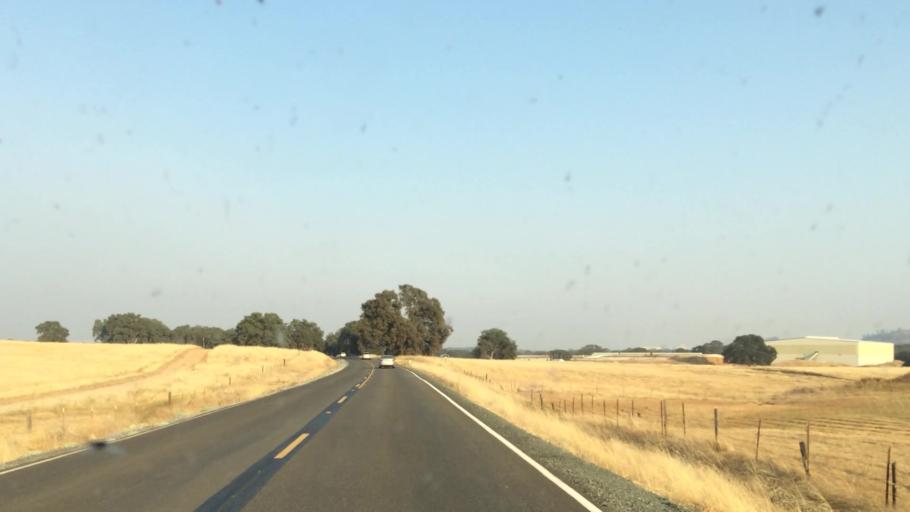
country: US
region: California
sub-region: Amador County
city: Ione
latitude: 38.4004
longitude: -121.0137
